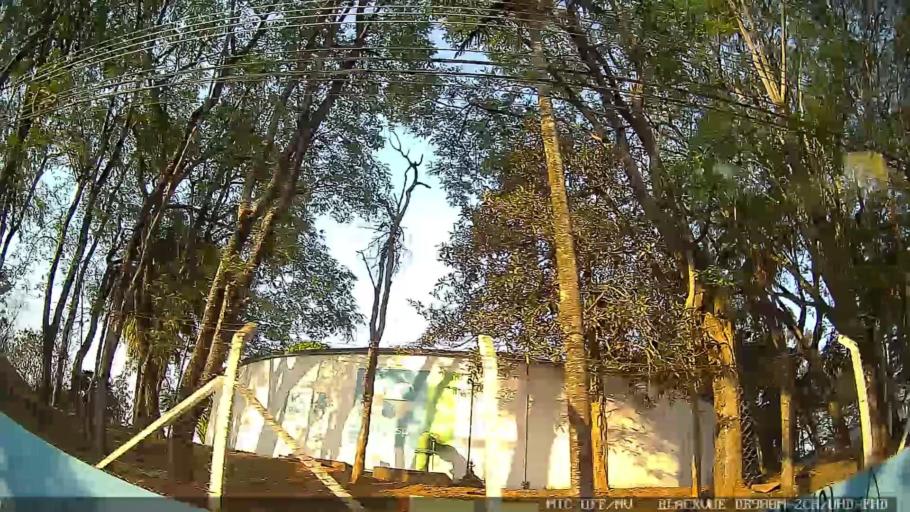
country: BR
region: Sao Paulo
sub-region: Itatiba
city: Itatiba
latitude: -23.0085
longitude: -46.8315
